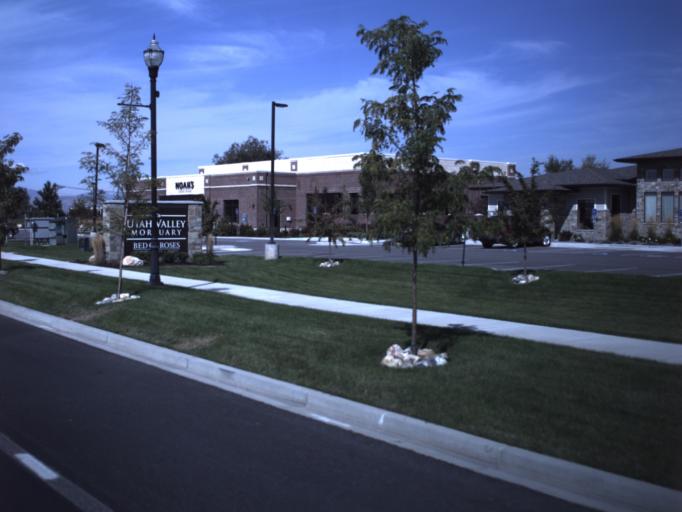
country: US
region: Utah
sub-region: Utah County
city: Pleasant Grove
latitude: 40.3507
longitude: -111.7566
